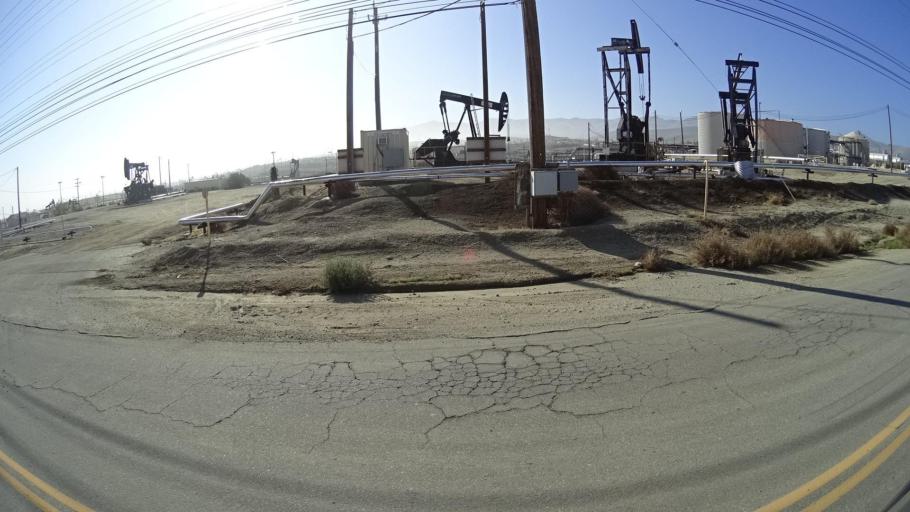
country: US
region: California
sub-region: Kern County
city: Taft Heights
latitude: 35.2231
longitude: -119.6163
